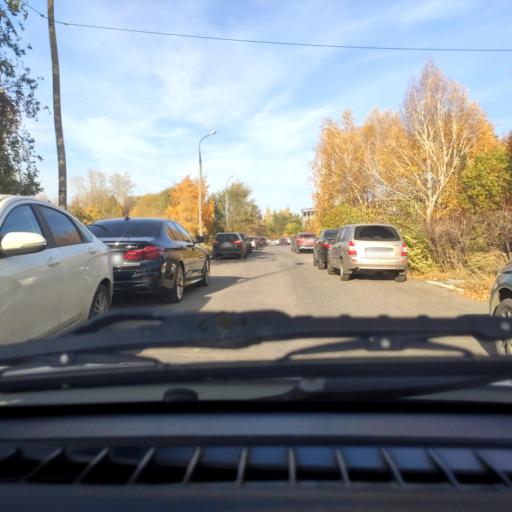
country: RU
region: Samara
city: Tol'yatti
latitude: 53.5519
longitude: 49.2698
